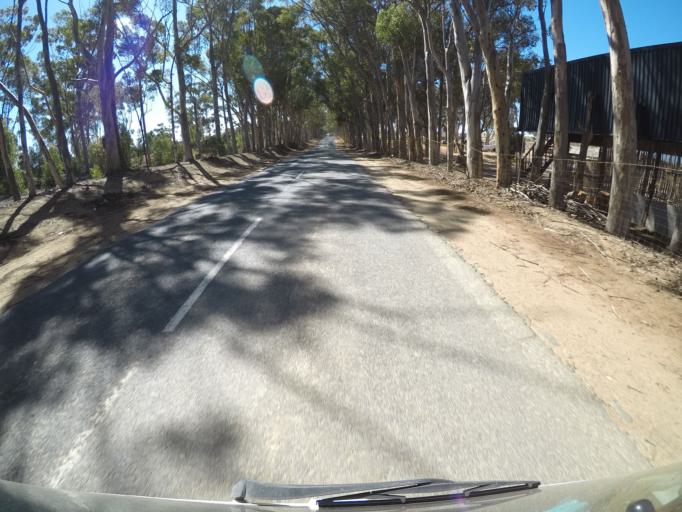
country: ZA
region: Western Cape
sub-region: City of Cape Town
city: Sunset Beach
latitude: -33.7622
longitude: 18.5522
